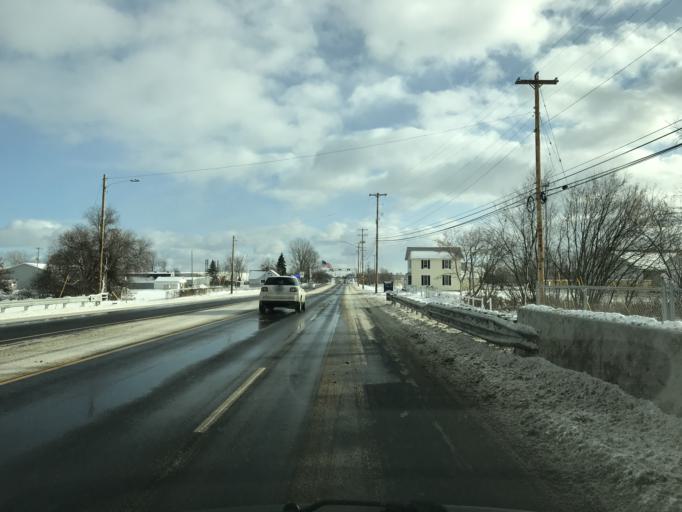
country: US
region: Michigan
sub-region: Kent County
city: Cutlerville
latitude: 42.8263
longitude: -85.6822
